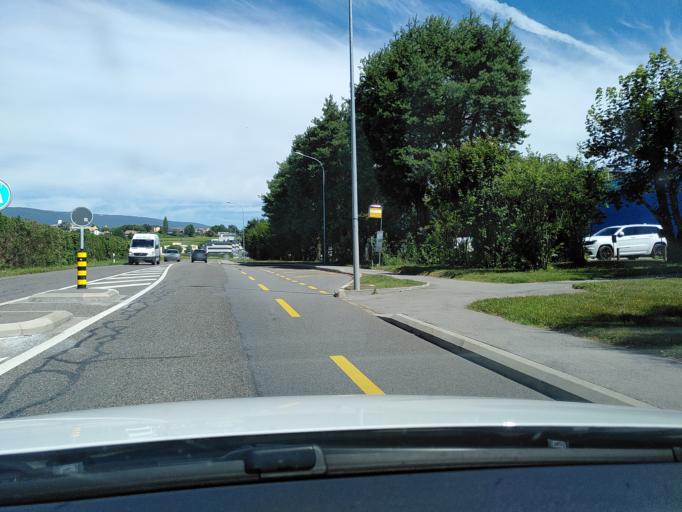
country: CH
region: Vaud
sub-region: Morges District
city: Aubonne
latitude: 46.4852
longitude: 6.4004
